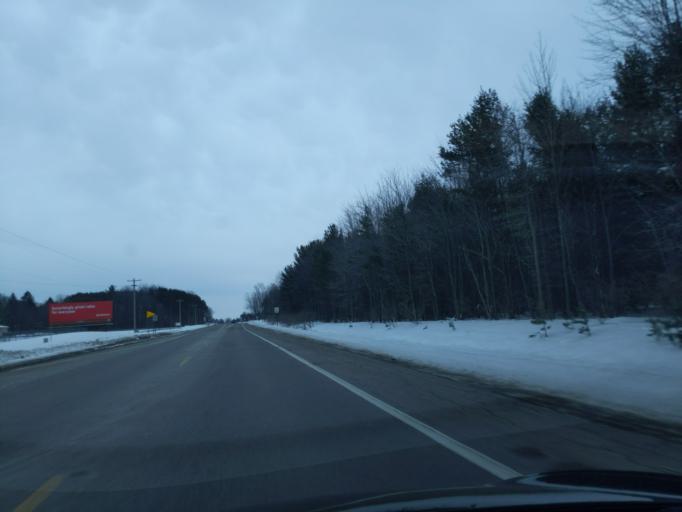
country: US
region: Michigan
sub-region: Muskegon County
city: Fruitport
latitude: 43.0741
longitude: -86.1007
